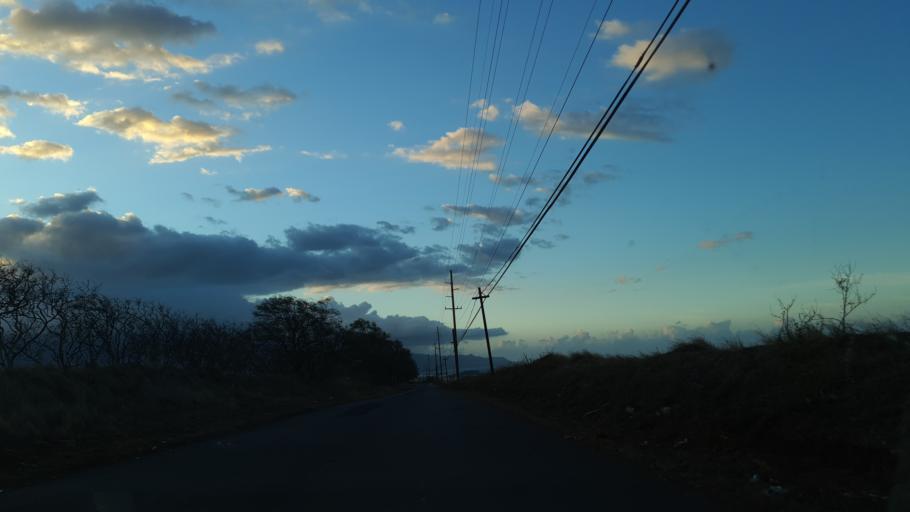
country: US
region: Hawaii
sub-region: Maui County
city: Kahului
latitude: 20.8619
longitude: -156.4281
